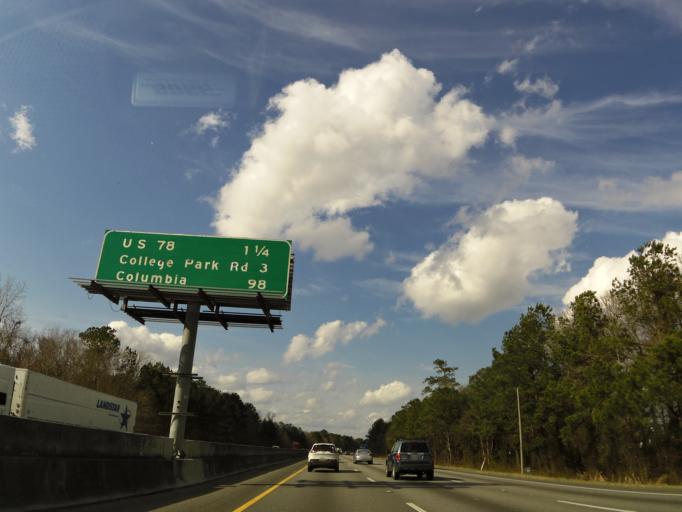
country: US
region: South Carolina
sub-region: Berkeley County
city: Goose Creek
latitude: 32.9585
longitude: -80.0690
